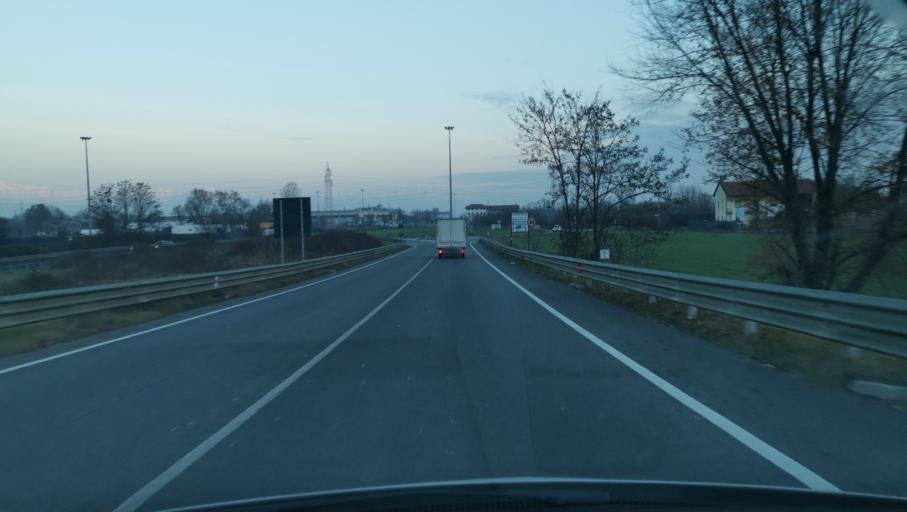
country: IT
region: Piedmont
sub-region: Provincia di Torino
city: Chivasso
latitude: 45.2114
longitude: 7.8902
